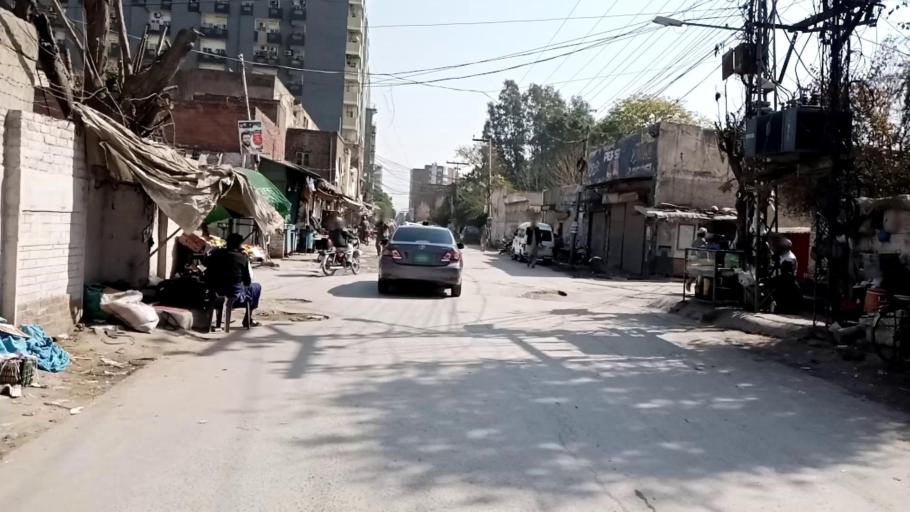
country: PK
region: Khyber Pakhtunkhwa
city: Peshawar
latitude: 33.9956
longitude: 71.5018
